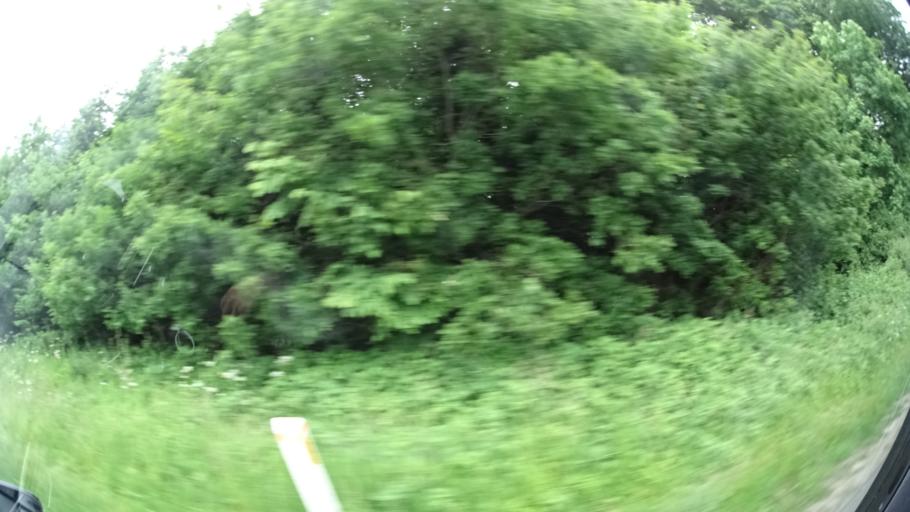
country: DK
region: Central Jutland
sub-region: Syddjurs Kommune
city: Hornslet
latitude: 56.3013
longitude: 10.3730
